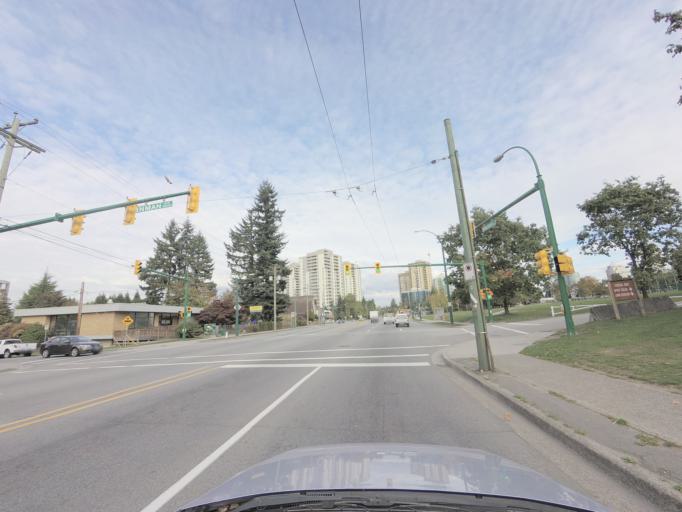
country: CA
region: British Columbia
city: Burnaby
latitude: 49.2327
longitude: -123.0161
